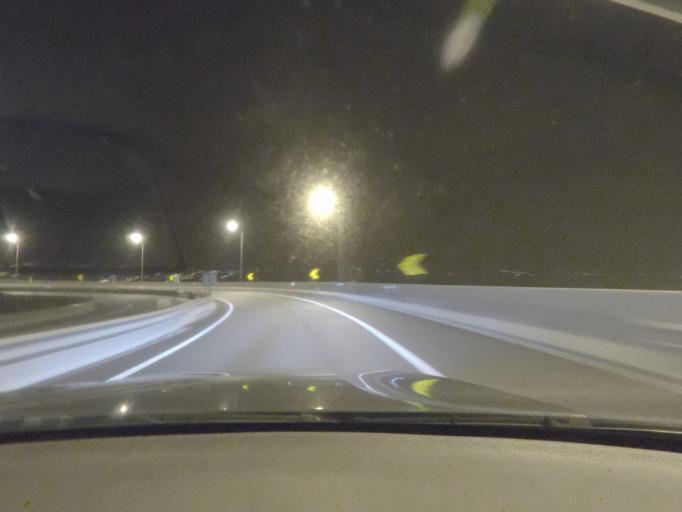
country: PT
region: Vila Real
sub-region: Vila Real
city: Vila Real
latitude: 41.2749
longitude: -7.7694
